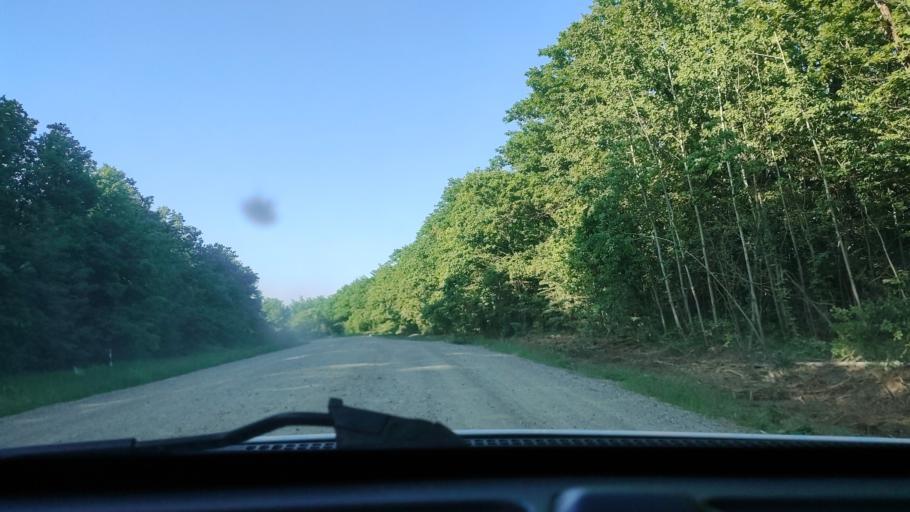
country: RU
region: Krasnodarskiy
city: Goryachiy Klyuch
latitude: 44.7065
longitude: 38.9913
